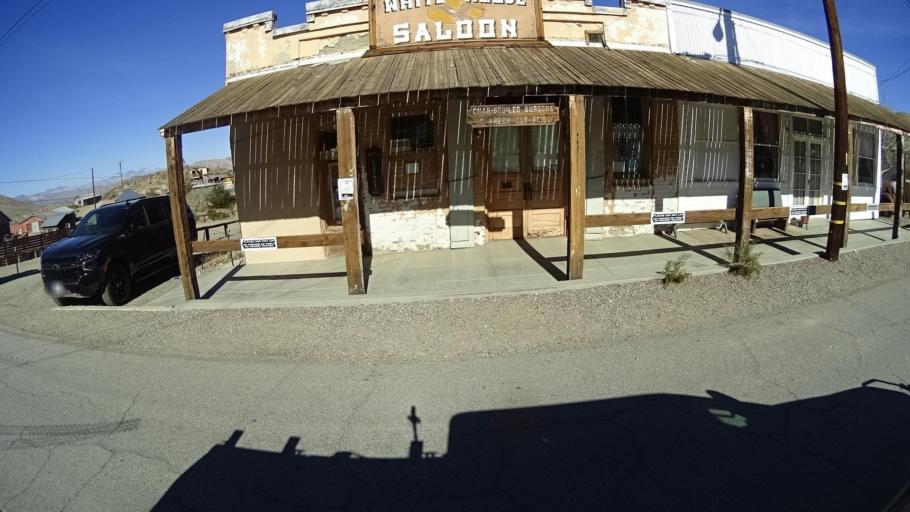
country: US
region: California
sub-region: Kern County
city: Ridgecrest
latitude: 35.3680
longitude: -117.6562
